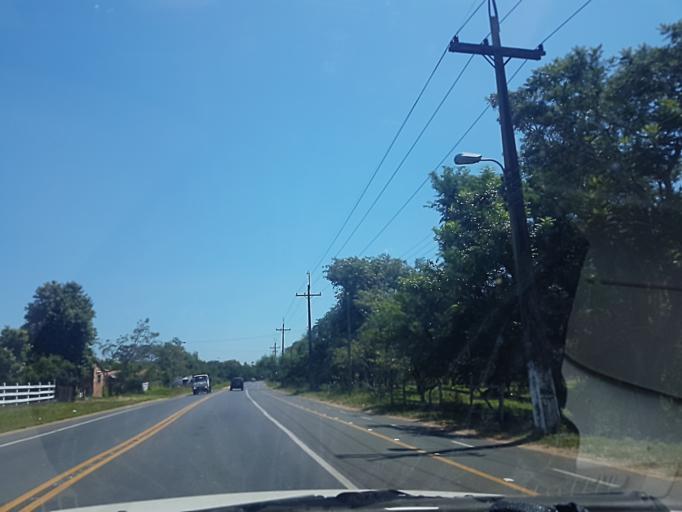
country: PY
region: Central
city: Aregua
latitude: -25.2330
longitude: -57.4199
